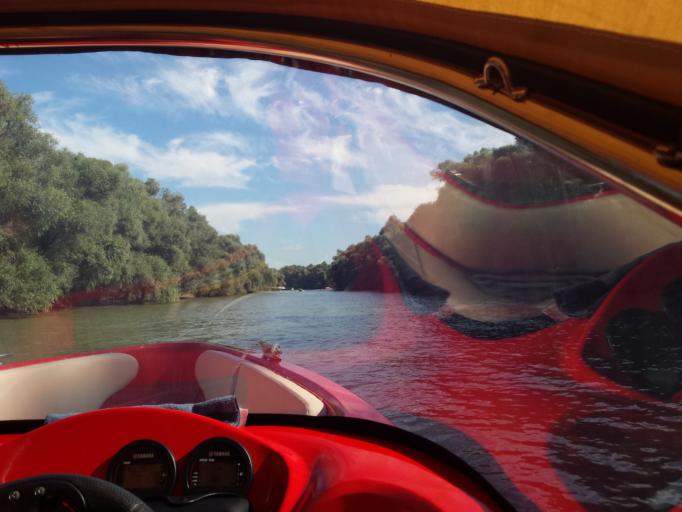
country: RO
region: Tulcea
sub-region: Comuna Pardina
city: Pardina
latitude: 45.2467
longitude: 28.9229
